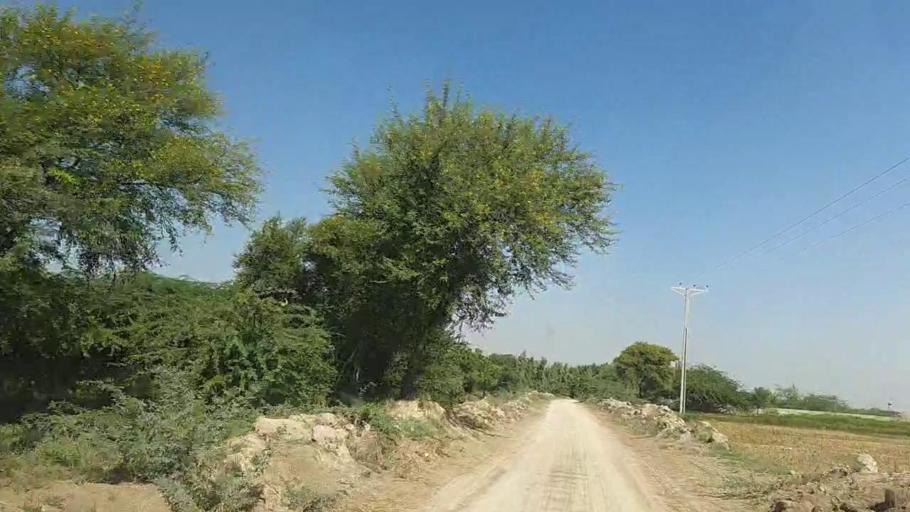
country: PK
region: Sindh
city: Daro Mehar
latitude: 24.7744
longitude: 68.1562
